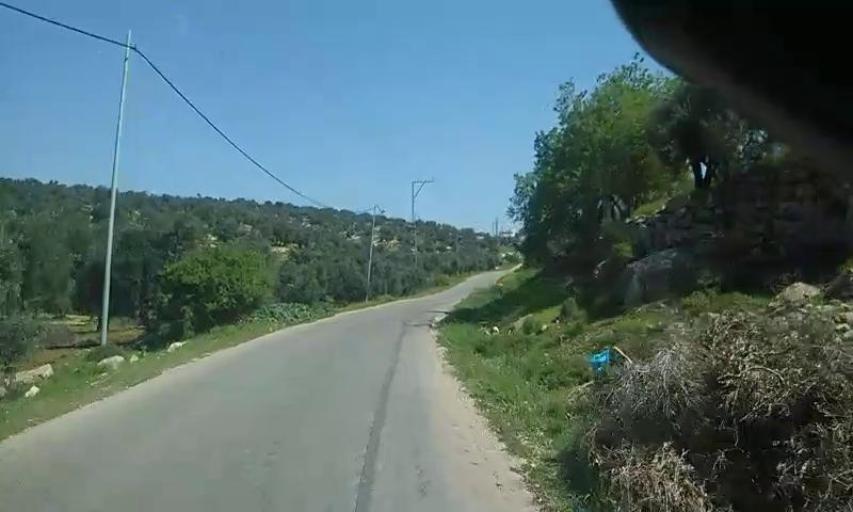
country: PS
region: West Bank
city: Al Majd
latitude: 31.4909
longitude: 34.9530
